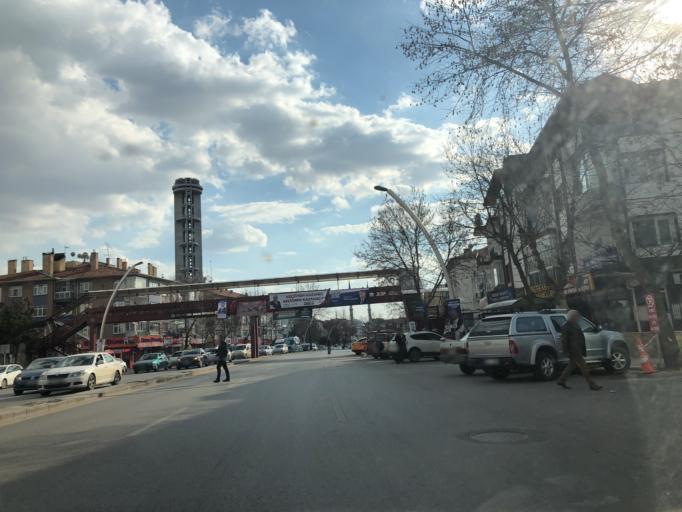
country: TR
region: Ankara
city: Mamak
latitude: 39.9880
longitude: 32.8658
